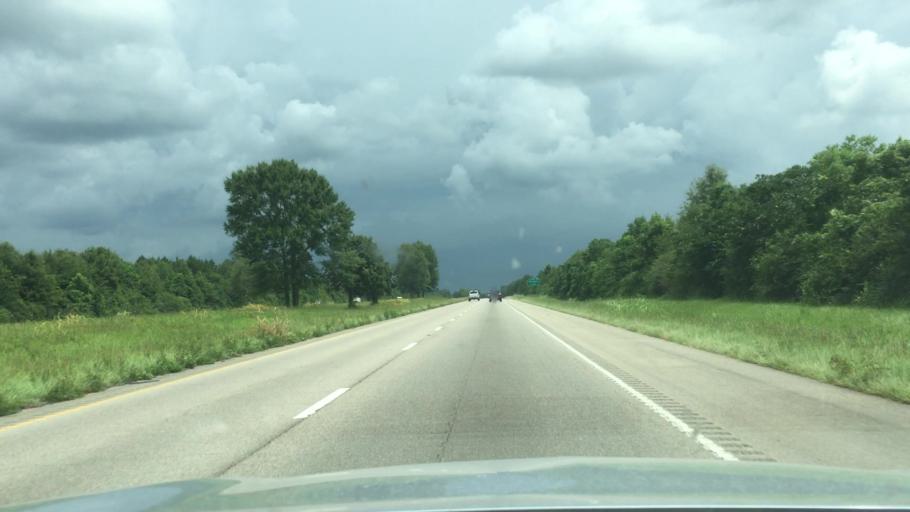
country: US
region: Mississippi
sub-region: Pearl River County
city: Carriere
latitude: 30.5828
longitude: -89.6278
